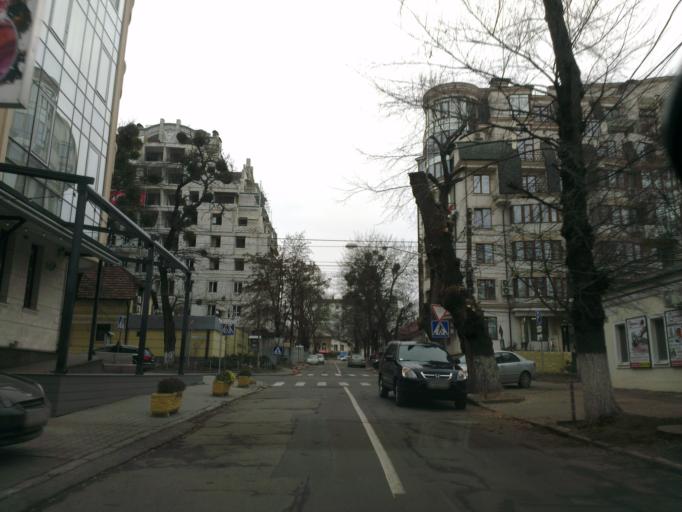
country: MD
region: Chisinau
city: Chisinau
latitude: 47.0169
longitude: 28.8272
